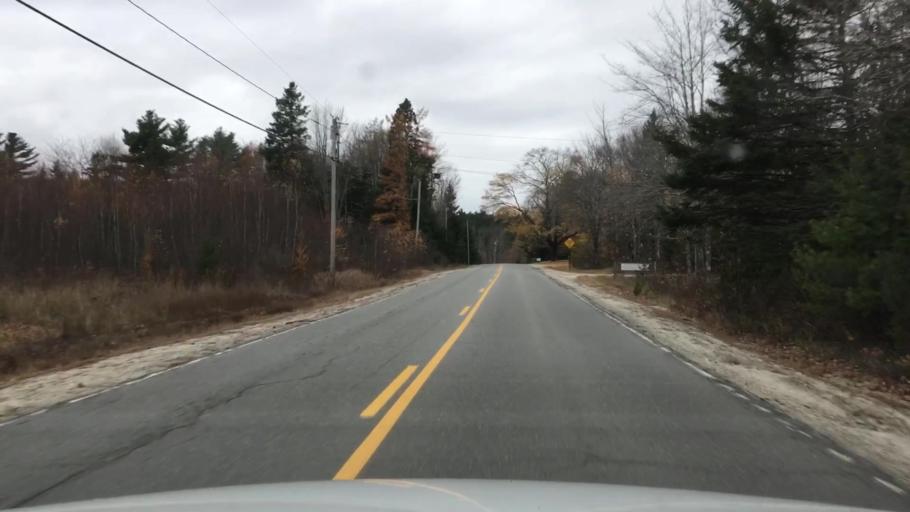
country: US
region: Maine
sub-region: Hancock County
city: Penobscot
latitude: 44.4212
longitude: -68.6193
